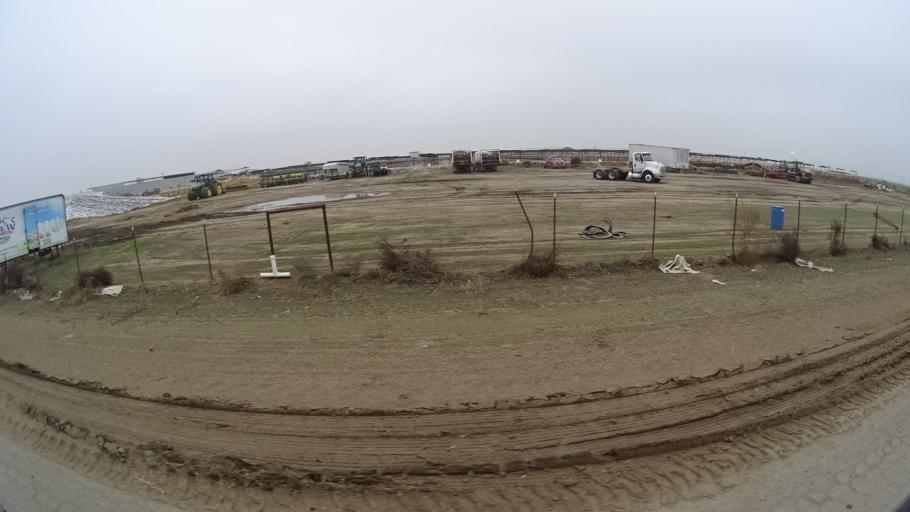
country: US
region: California
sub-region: Kern County
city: Wasco
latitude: 35.7126
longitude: -119.4194
